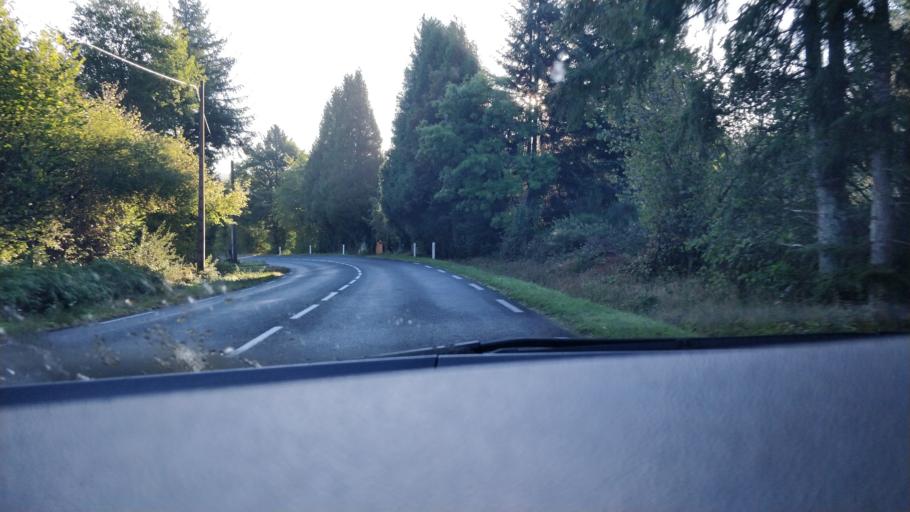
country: FR
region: Limousin
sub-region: Departement de la Haute-Vienne
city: Sauviat-sur-Vige
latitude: 45.9360
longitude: 1.6532
